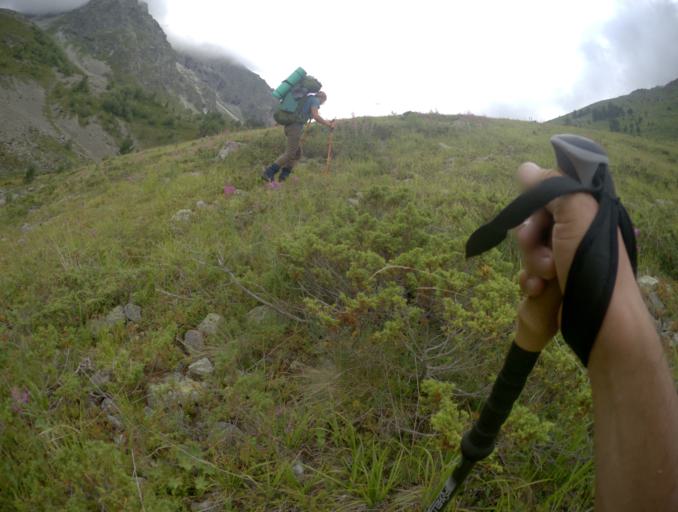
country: RU
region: Karachayevo-Cherkesiya
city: Uchkulan
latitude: 43.3389
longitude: 42.1333
